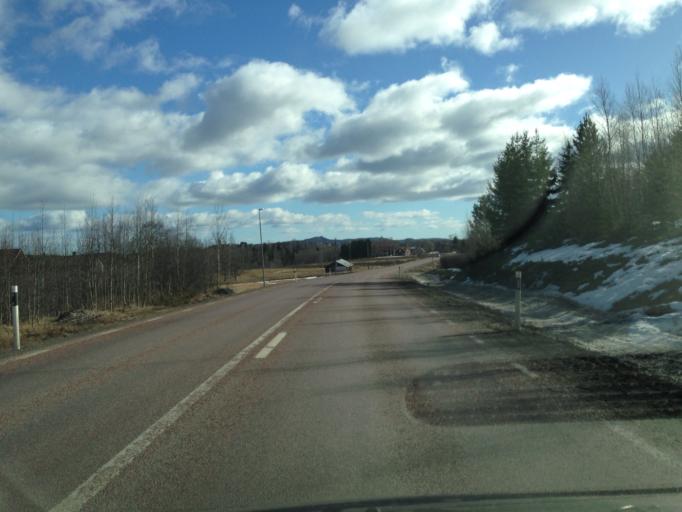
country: SE
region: Gaevleborg
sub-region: Ljusdals Kommun
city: Farila
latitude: 61.7999
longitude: 15.8077
